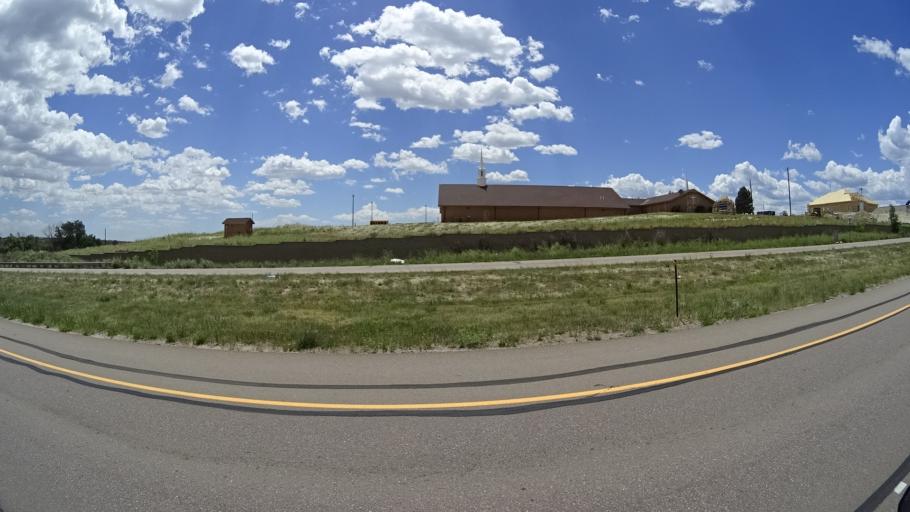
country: US
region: Colorado
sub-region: El Paso County
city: Black Forest
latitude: 38.9412
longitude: -104.6979
